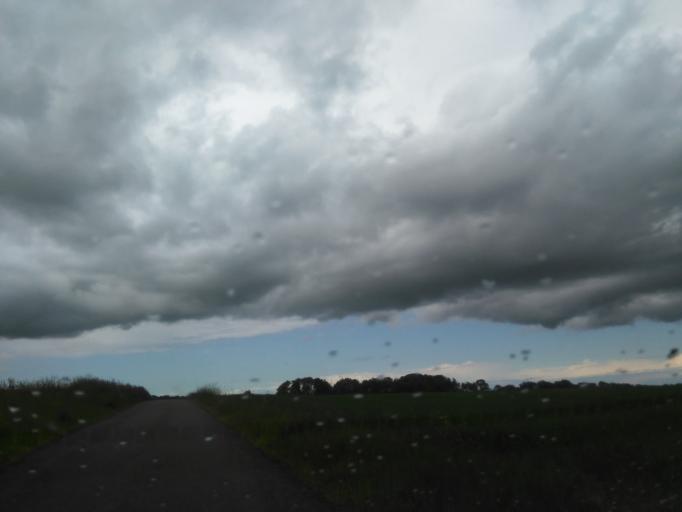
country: DK
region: Capital Region
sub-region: Bornholm Kommune
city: Nexo
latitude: 55.0946
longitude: 15.1406
